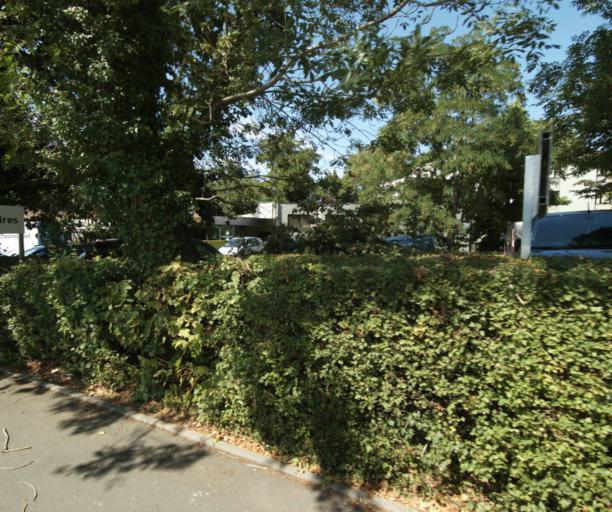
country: FR
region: Nord-Pas-de-Calais
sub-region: Departement du Nord
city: Neuville-en-Ferrain
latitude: 50.7585
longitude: 3.1488
